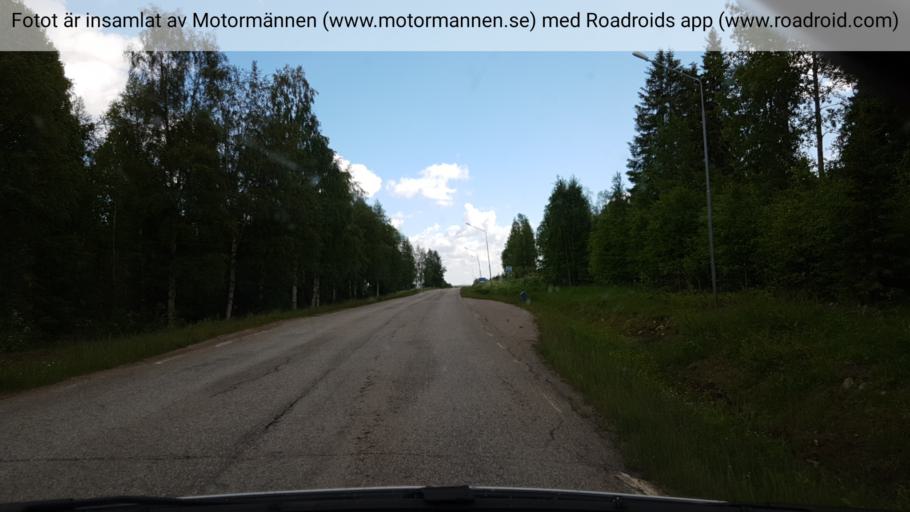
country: FI
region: Lapland
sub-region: Torniolaakso
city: Ylitornio
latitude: 66.1870
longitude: 23.7470
